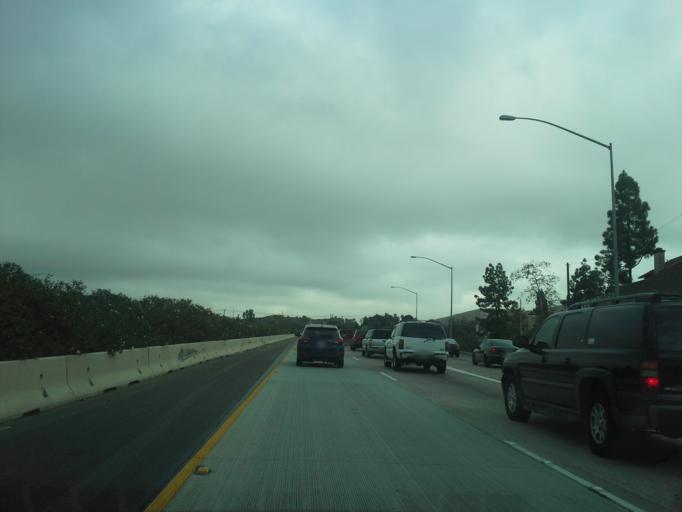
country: US
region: California
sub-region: San Diego County
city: Granite Hills
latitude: 32.8090
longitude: -116.9188
